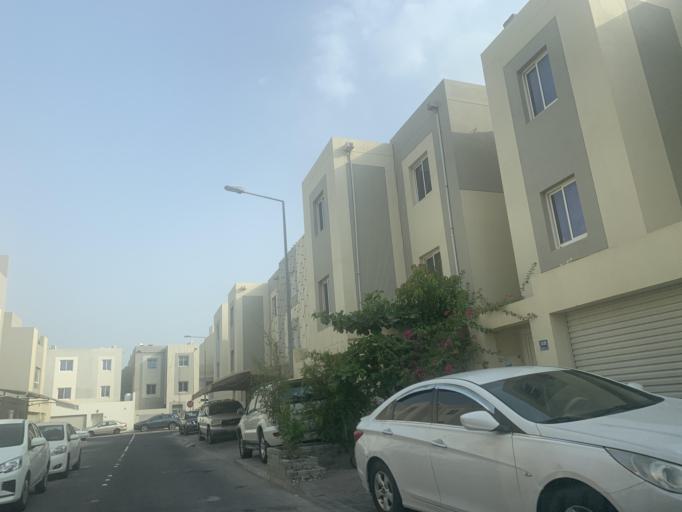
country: BH
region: Manama
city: Jidd Hafs
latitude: 26.2256
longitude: 50.4530
